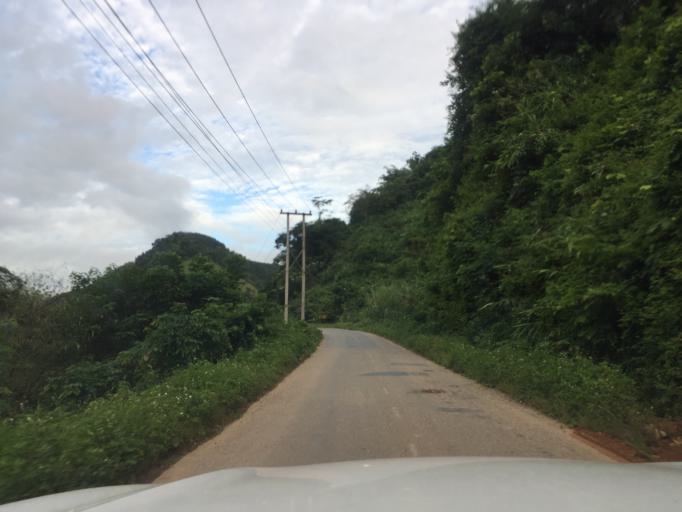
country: LA
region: Phongsali
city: Khoa
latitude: 21.1039
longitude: 102.3007
